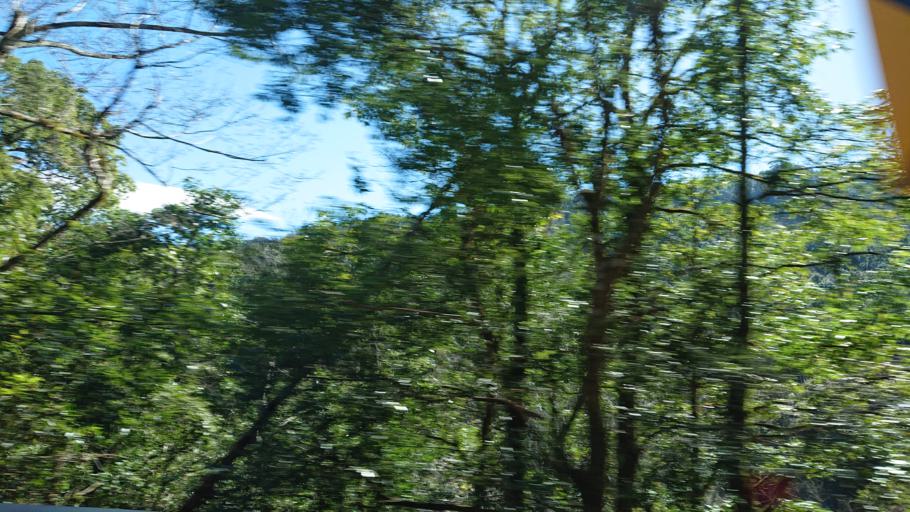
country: TW
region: Taiwan
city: Daxi
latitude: 24.4055
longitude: 121.3605
